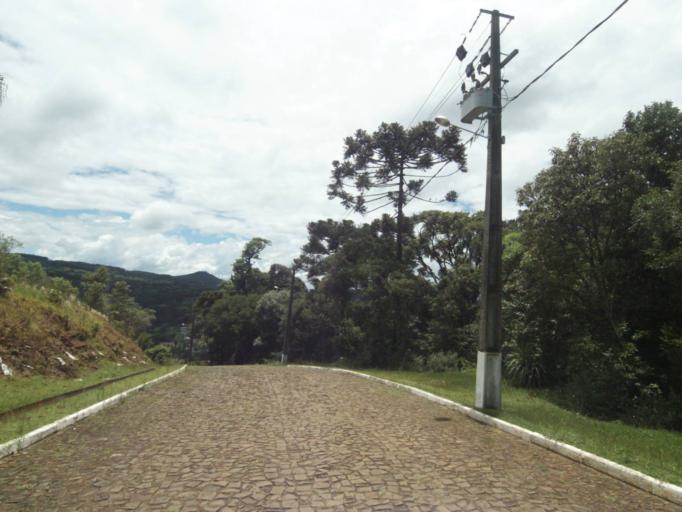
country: BR
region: Parana
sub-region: Uniao Da Vitoria
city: Uniao da Vitoria
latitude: -26.1615
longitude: -51.5579
